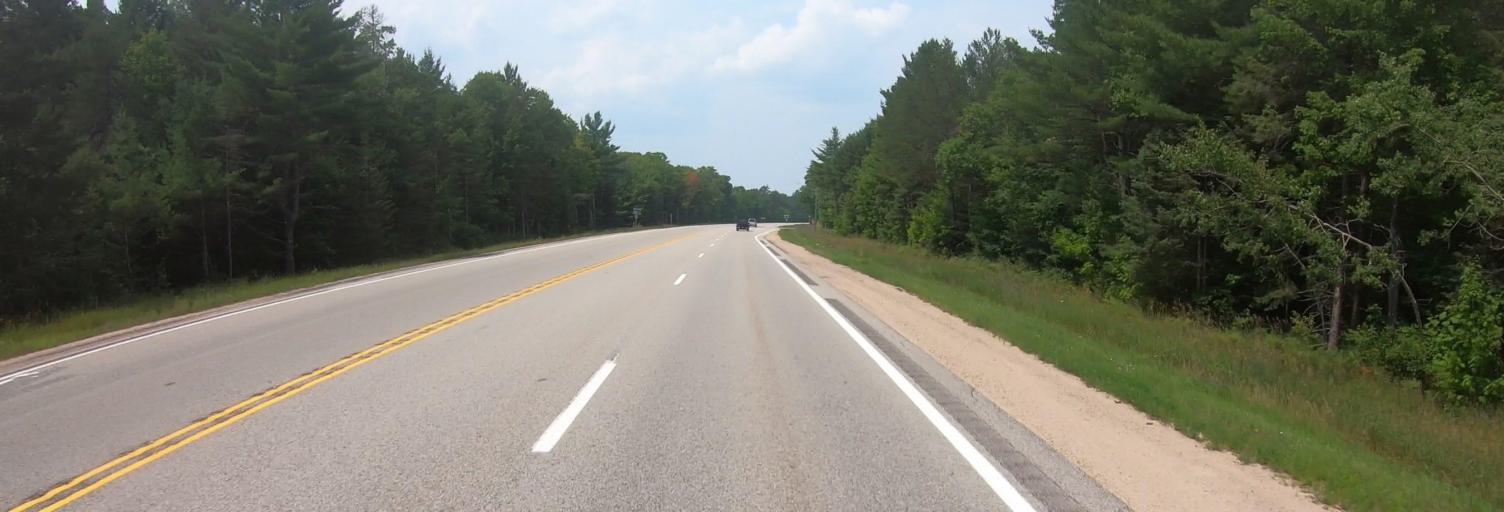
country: US
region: Michigan
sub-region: Alger County
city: Munising
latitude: 46.3482
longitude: -86.4877
